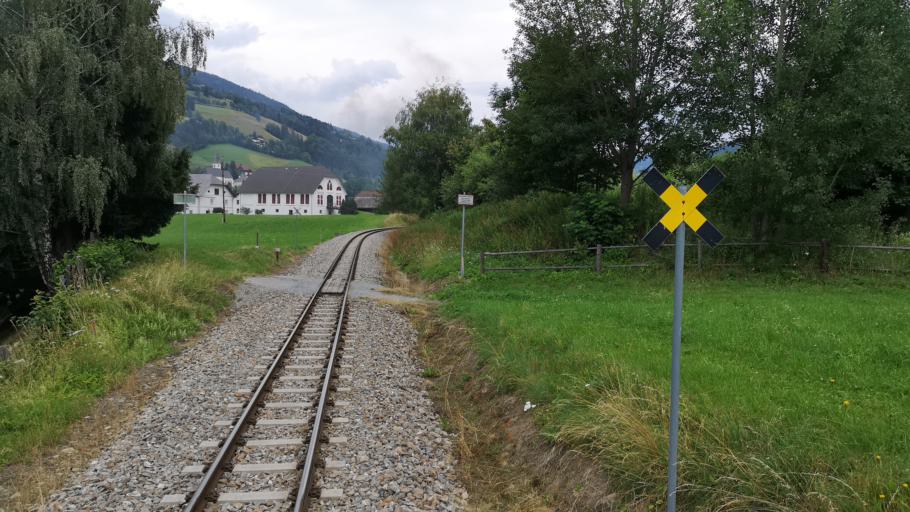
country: AT
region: Styria
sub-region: Politischer Bezirk Murau
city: Stadl an der Mur
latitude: 47.0833
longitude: 13.9782
